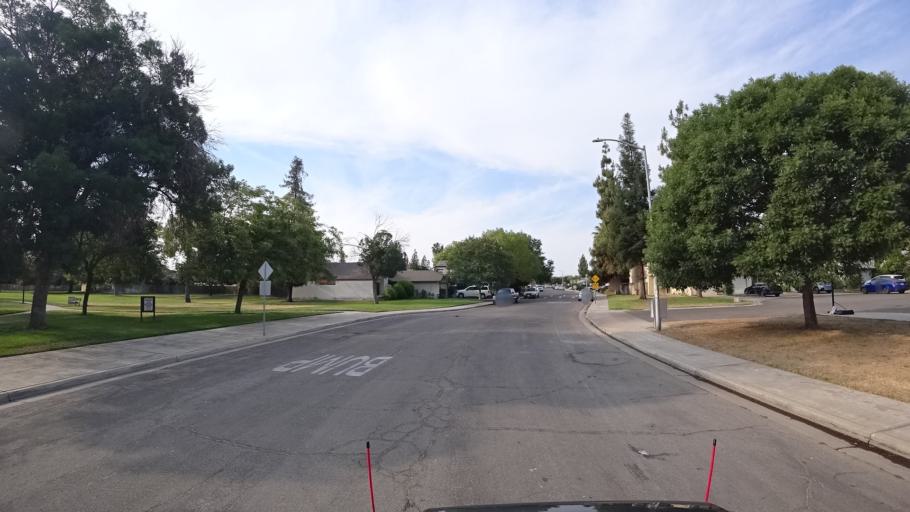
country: US
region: California
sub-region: Fresno County
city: West Park
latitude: 36.7739
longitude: -119.8596
